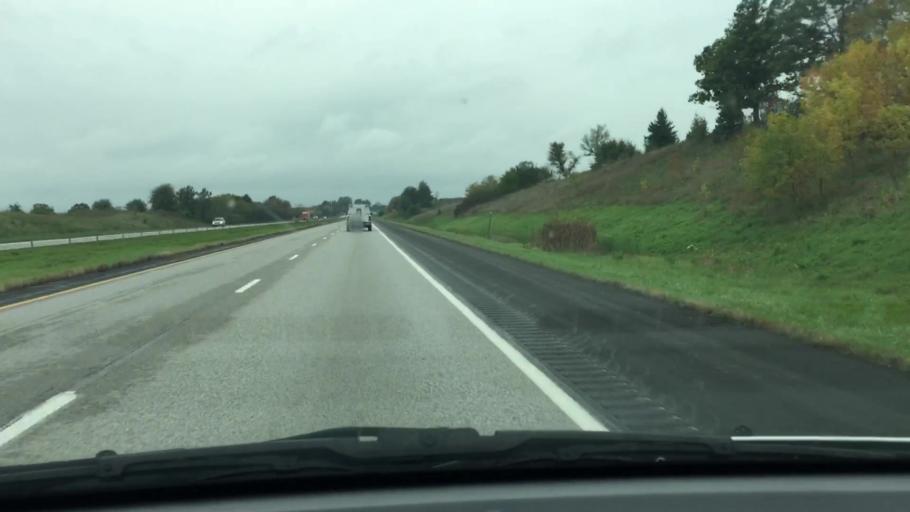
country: US
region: Iowa
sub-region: Johnson County
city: Tiffin
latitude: 41.6904
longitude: -91.7641
